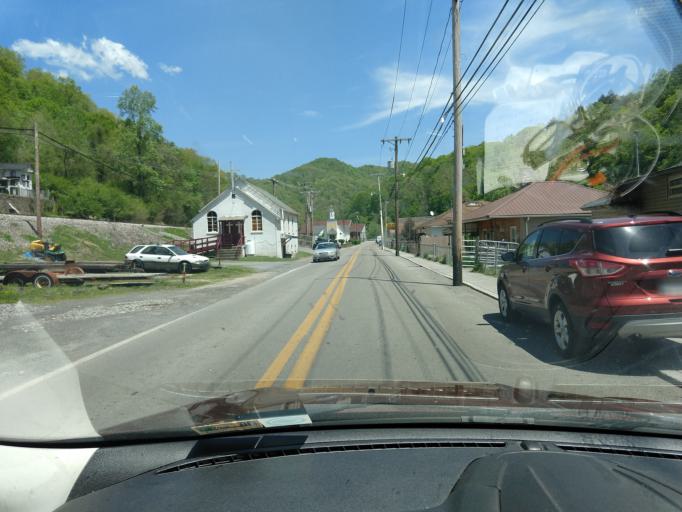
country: US
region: West Virginia
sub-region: McDowell County
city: Welch
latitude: 37.3019
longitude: -81.6821
